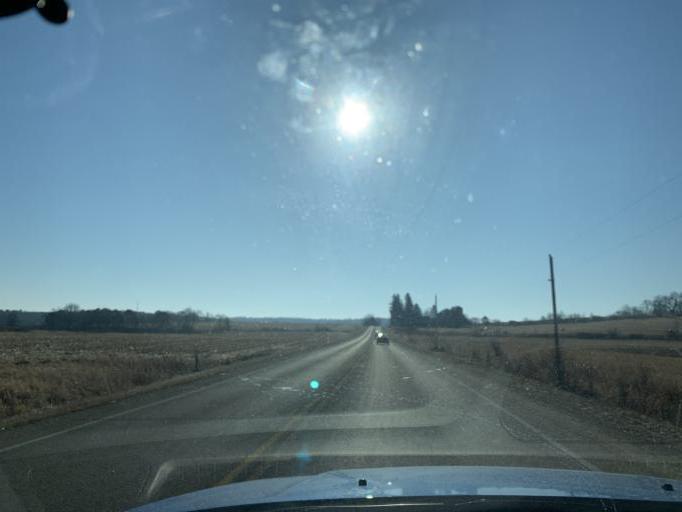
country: US
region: Wisconsin
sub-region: Dane County
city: Belleville
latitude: 42.8767
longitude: -89.5606
